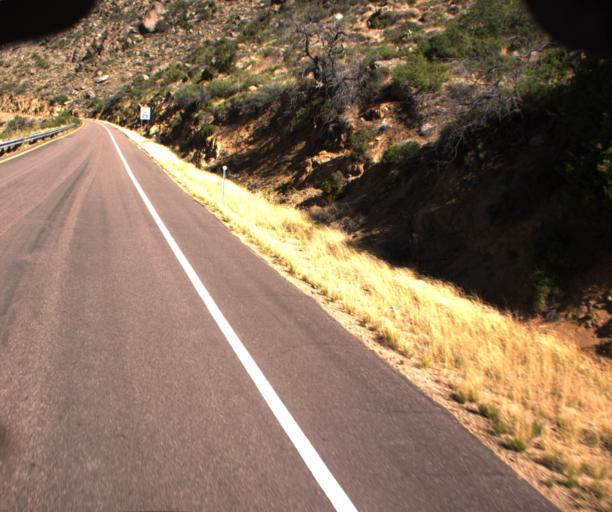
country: US
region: Arizona
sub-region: Yavapai County
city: Congress
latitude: 34.2022
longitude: -112.7658
